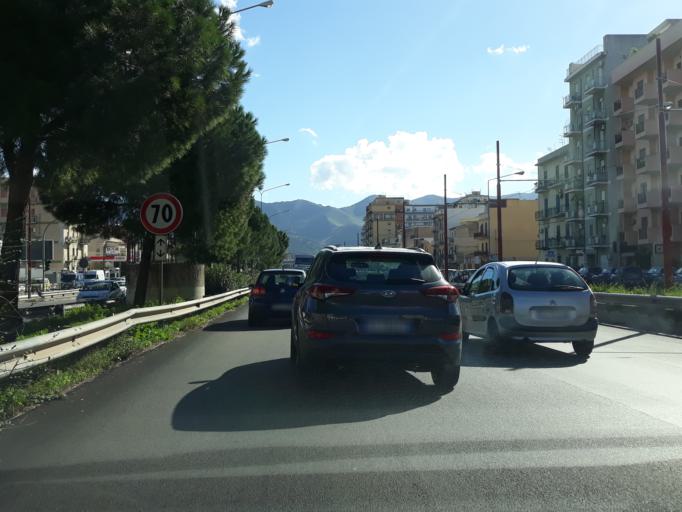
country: IT
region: Sicily
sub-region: Palermo
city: Palermo
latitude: 38.1132
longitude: 13.3294
